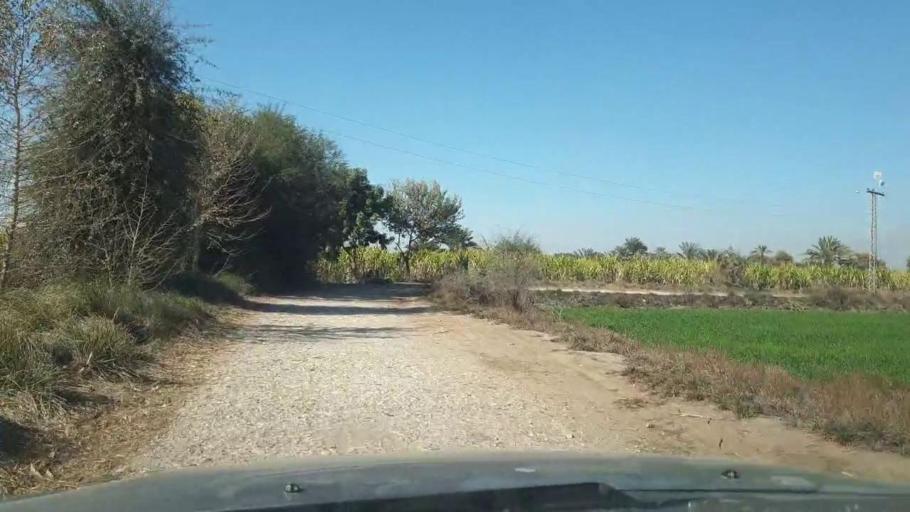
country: PK
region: Sindh
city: Ghotki
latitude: 28.0546
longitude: 69.2402
